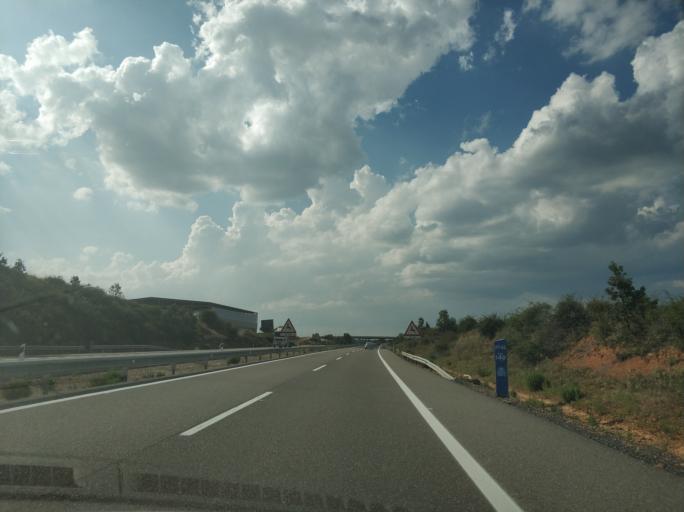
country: ES
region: Castille and Leon
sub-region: Provincia de Leon
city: Valverde de la Virgen
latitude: 42.5869
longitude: -5.6807
